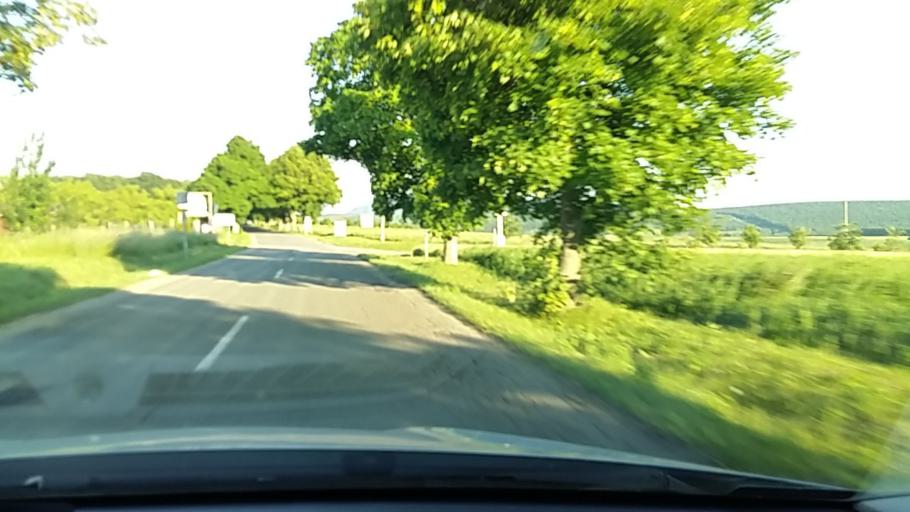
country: HU
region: Nograd
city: Diosjeno
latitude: 47.8957
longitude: 19.0819
